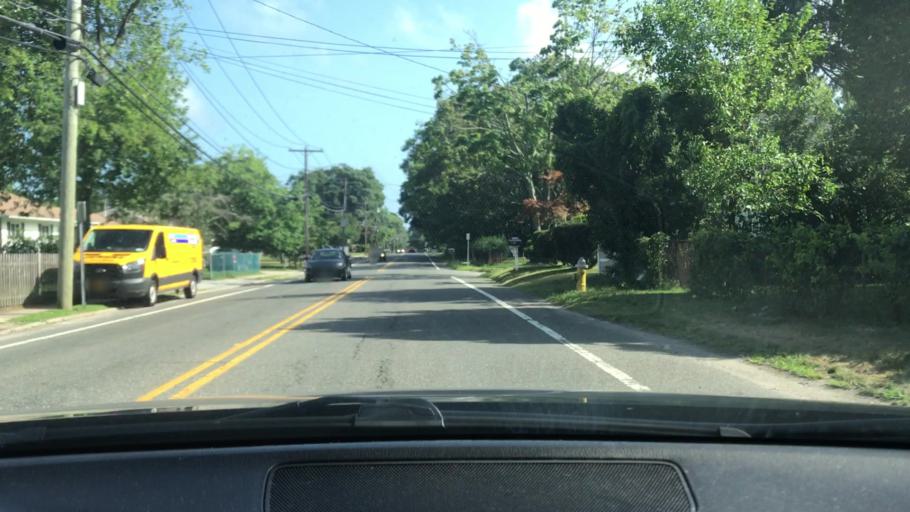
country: US
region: New York
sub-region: Suffolk County
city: Holbrook
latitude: 40.8301
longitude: -73.0815
